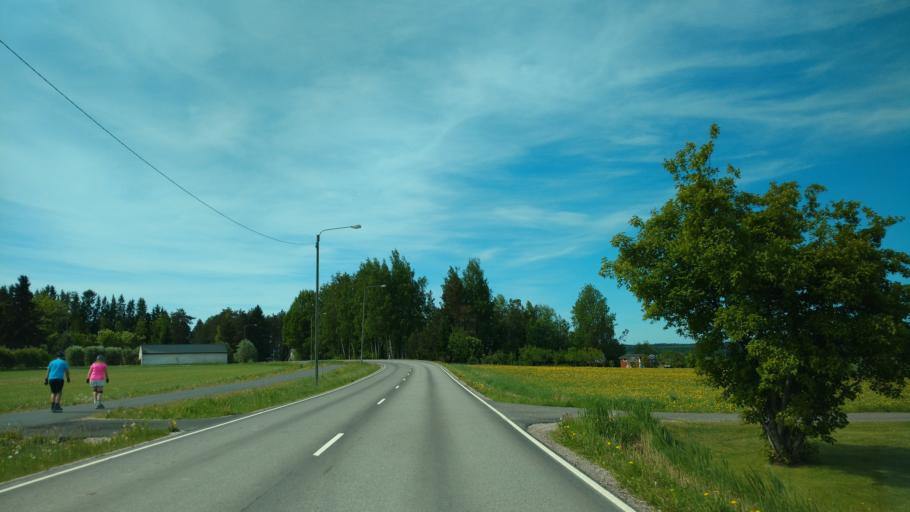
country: FI
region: Varsinais-Suomi
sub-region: Salo
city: Pertteli
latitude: 60.4254
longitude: 23.2035
